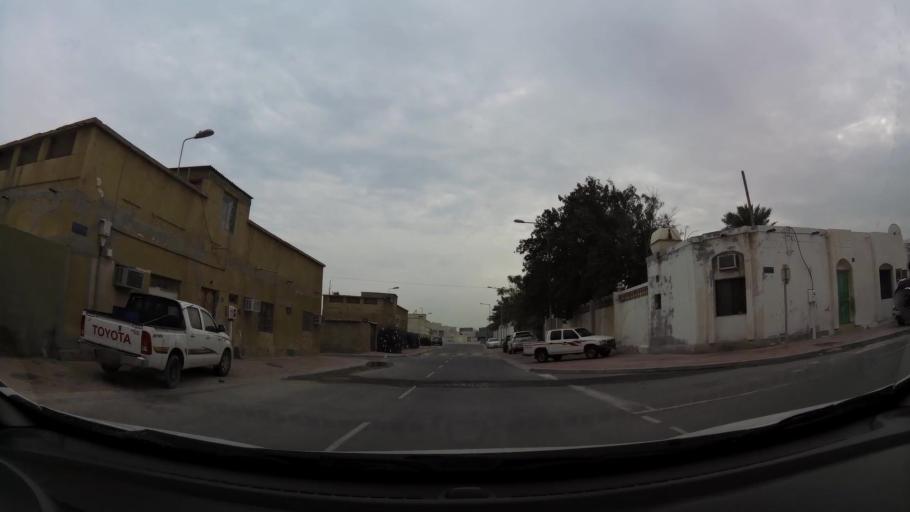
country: BH
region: Northern
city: Ar Rifa'
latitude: 26.0555
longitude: 50.6171
